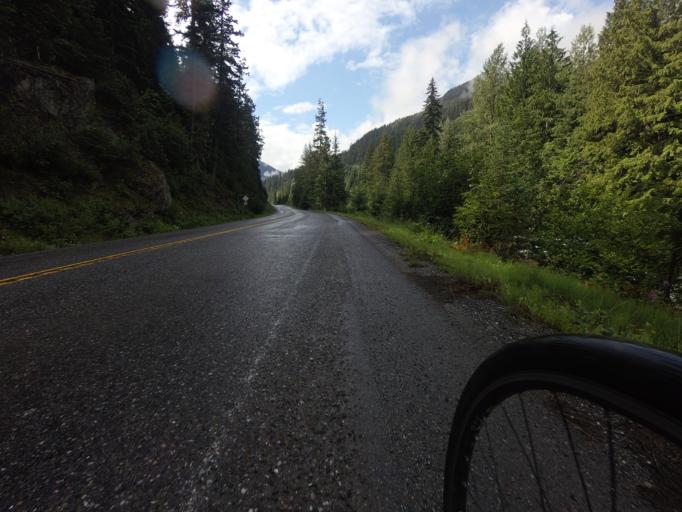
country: CA
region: British Columbia
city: Lillooet
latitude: 50.4612
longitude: -122.2493
